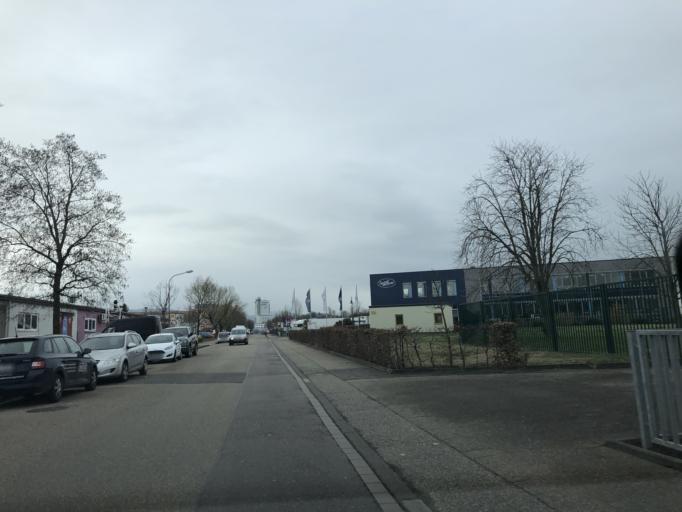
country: DE
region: Baden-Wuerttemberg
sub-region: Karlsruhe Region
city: Ettlingen
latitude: 48.9472
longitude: 8.3769
